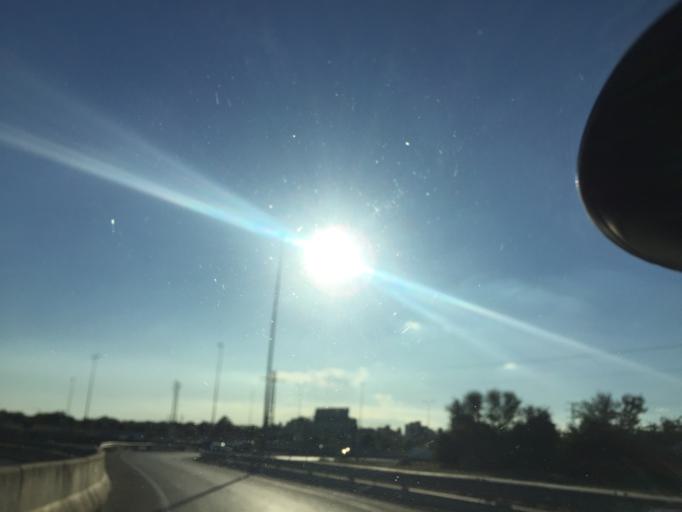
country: ES
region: Andalusia
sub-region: Provincia de Sevilla
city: Sevilla
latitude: 37.3609
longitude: -5.9560
